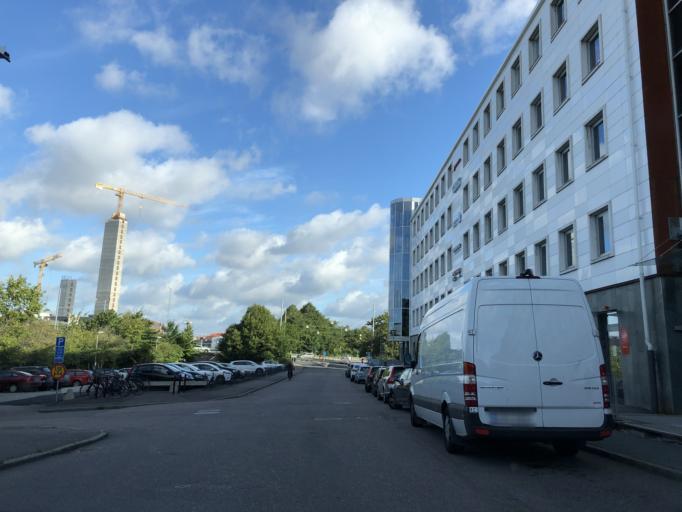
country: SE
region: Vaestra Goetaland
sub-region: Goteborg
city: Goeteborg
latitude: 57.7081
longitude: 11.9973
